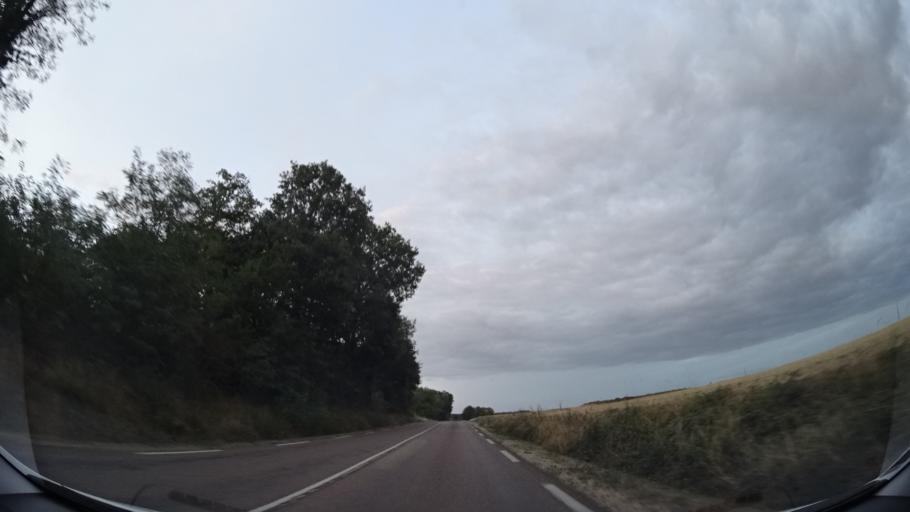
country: FR
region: Bourgogne
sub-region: Departement de l'Yonne
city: Cezy
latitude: 47.9378
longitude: 3.2616
